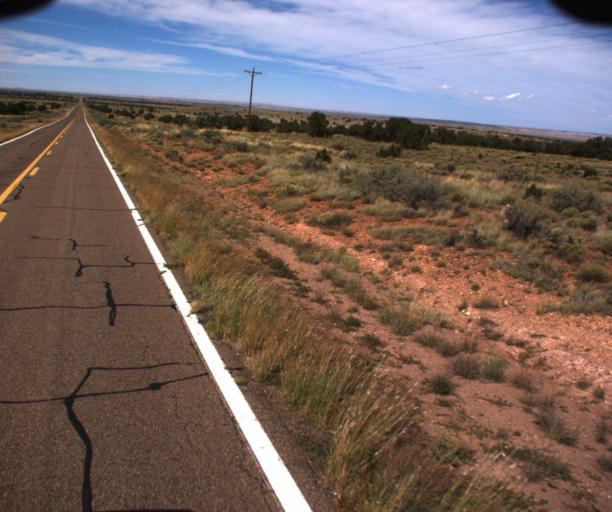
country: US
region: Arizona
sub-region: Apache County
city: Saint Johns
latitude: 34.5598
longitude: -109.6284
